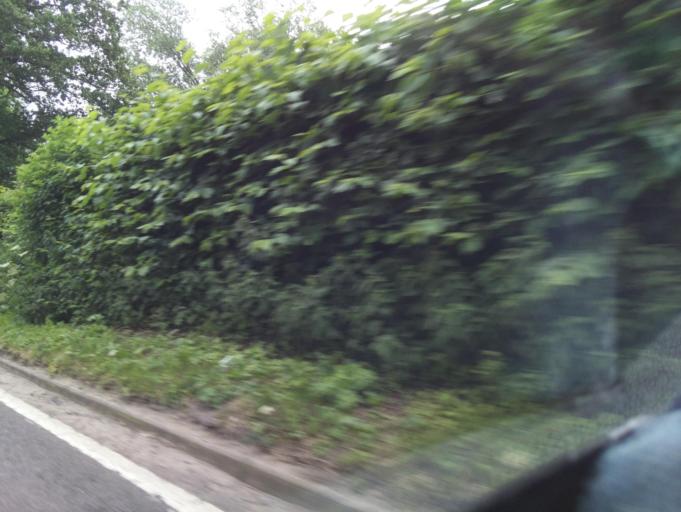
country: GB
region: England
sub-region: Derbyshire
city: Etwall
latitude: 52.9481
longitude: -1.5750
